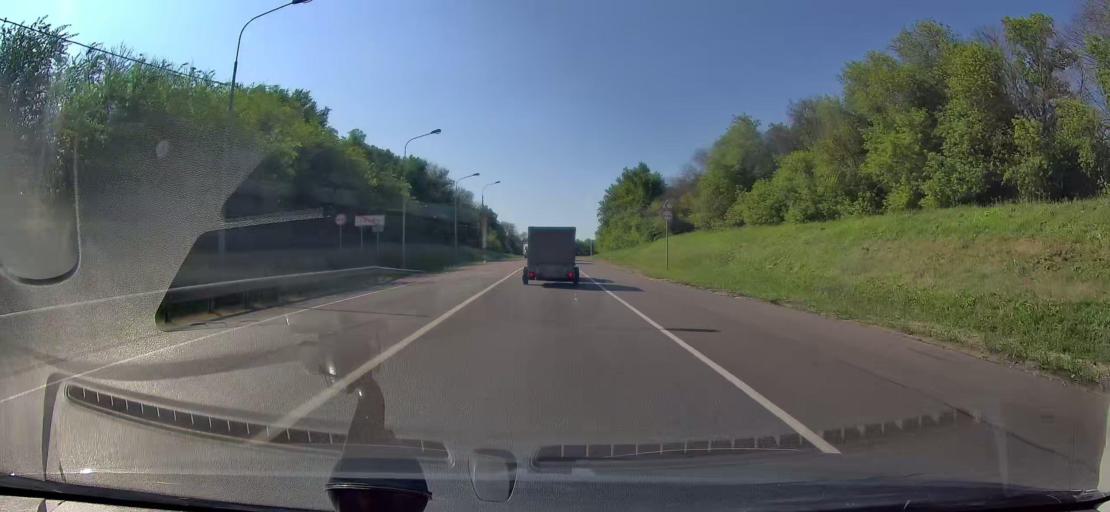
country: RU
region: Orjol
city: Kromy
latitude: 52.6165
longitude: 35.7615
